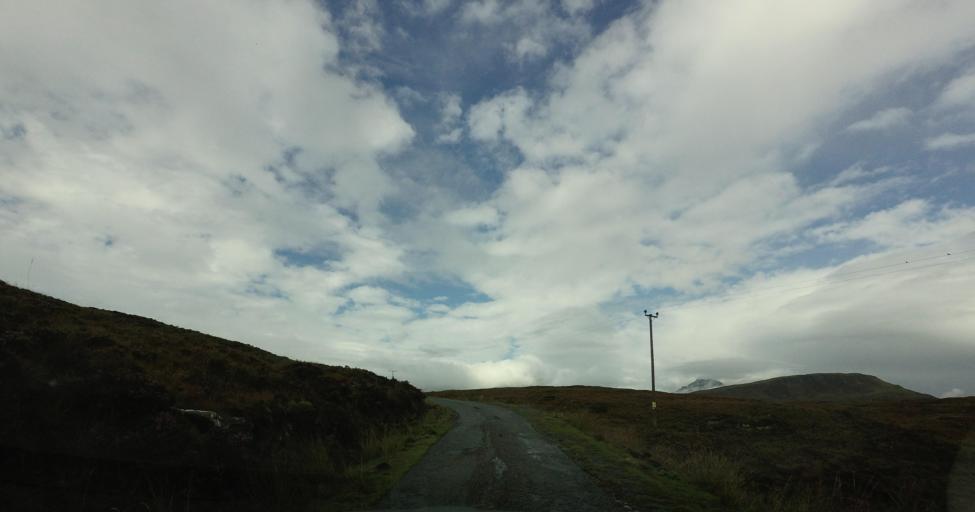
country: GB
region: Scotland
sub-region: Highland
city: Isle of Skye
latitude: 57.1435
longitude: -6.0784
